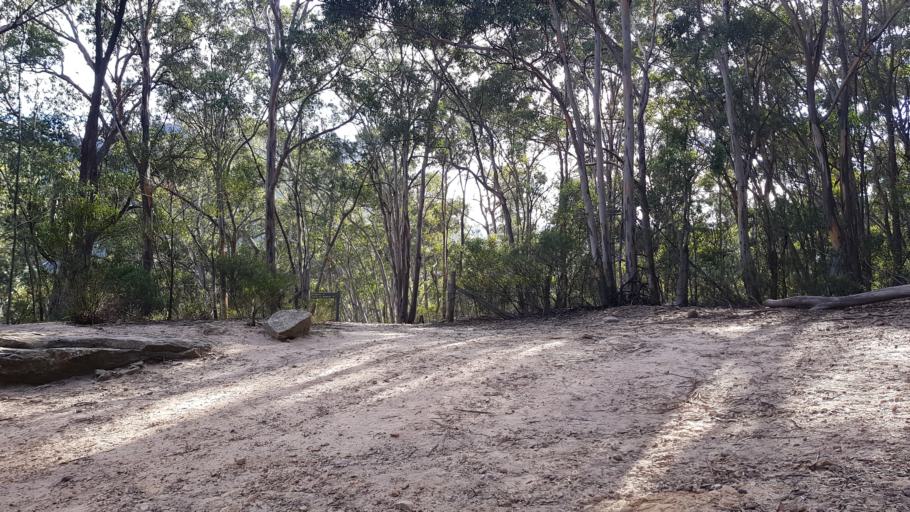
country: AU
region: New South Wales
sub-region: Lithgow
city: Lithgow
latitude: -33.2213
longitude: 150.2297
